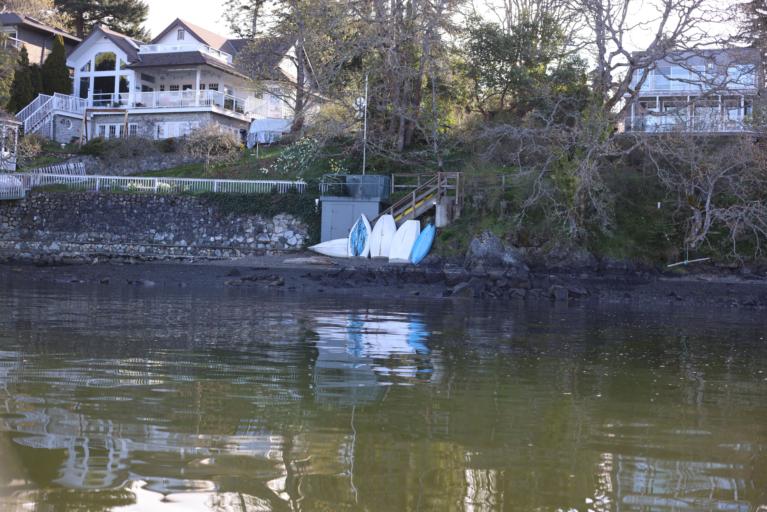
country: CA
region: British Columbia
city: North Saanich
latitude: 48.5753
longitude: -123.4657
